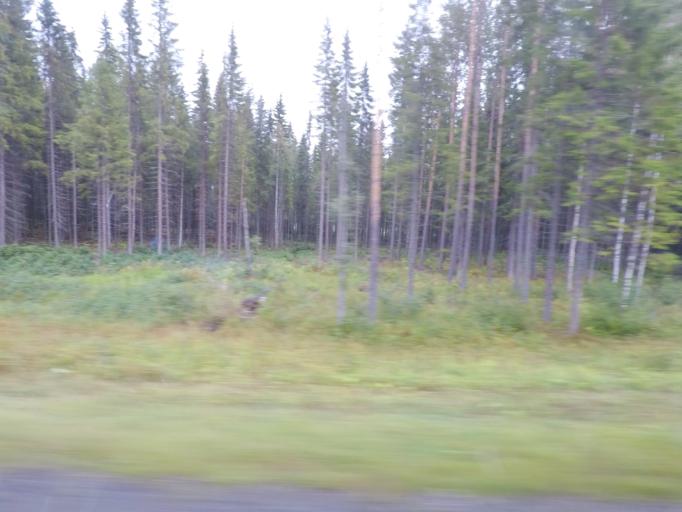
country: FI
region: Southern Savonia
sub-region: Pieksaemaeki
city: Juva
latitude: 61.9802
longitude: 27.8035
